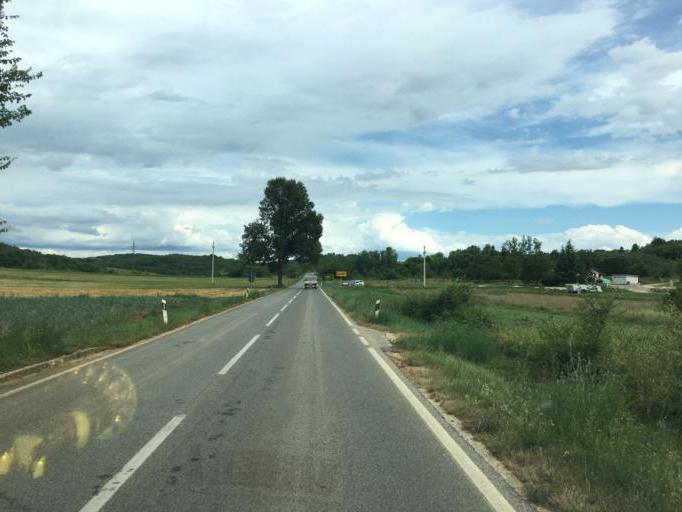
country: HR
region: Istarska
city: Karojba
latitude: 45.2752
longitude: 13.8506
